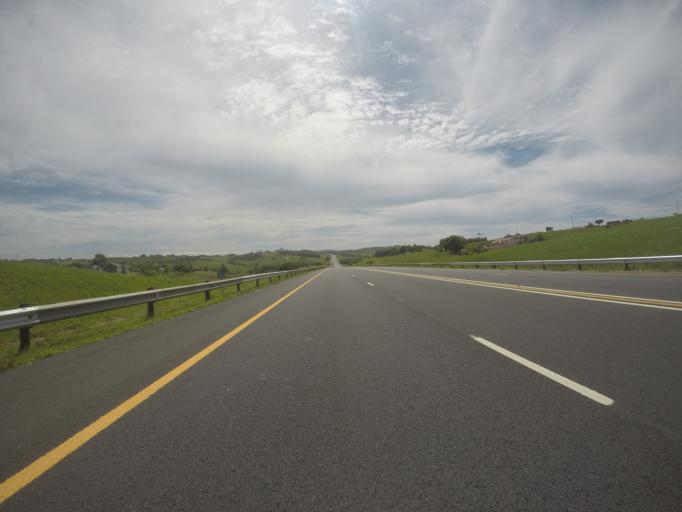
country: ZA
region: KwaZulu-Natal
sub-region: iLembe District Municipality
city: Mandeni
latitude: -29.1721
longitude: 31.5160
